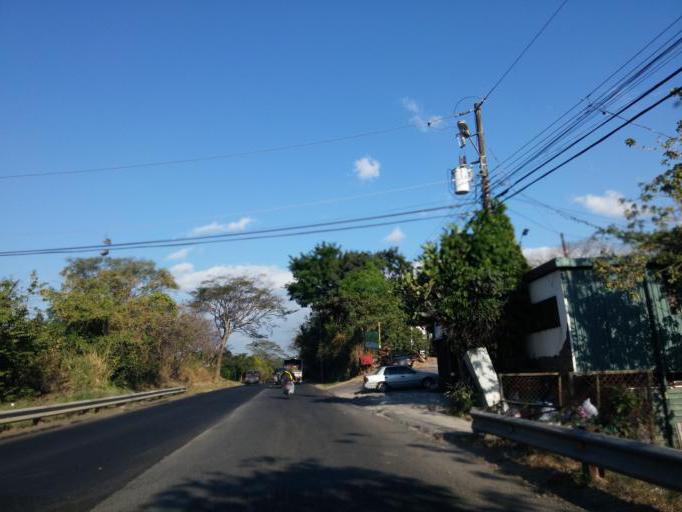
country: CR
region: Heredia
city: Colon
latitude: 9.9336
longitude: -84.2360
